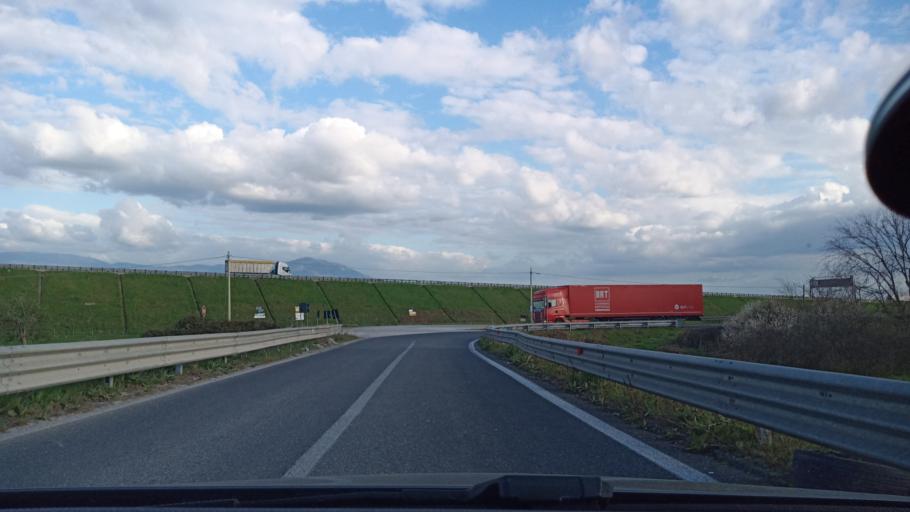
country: IT
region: Latium
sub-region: Citta metropolitana di Roma Capitale
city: Fiano Romano
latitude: 42.1482
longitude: 12.6220
